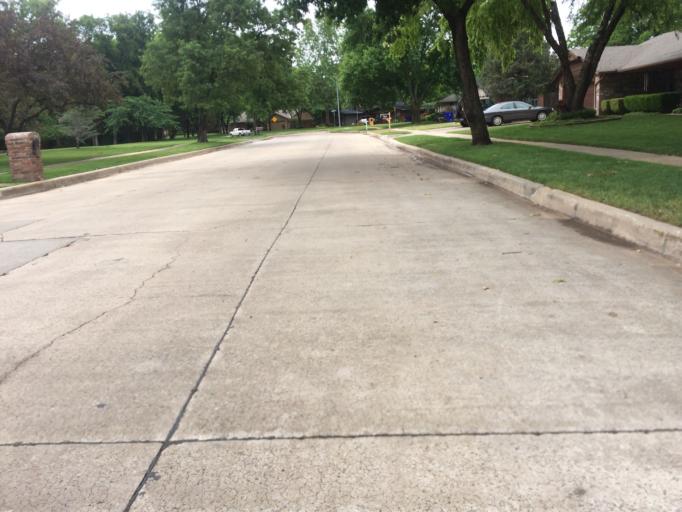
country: US
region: Oklahoma
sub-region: Cleveland County
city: Norman
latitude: 35.1849
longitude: -97.4560
